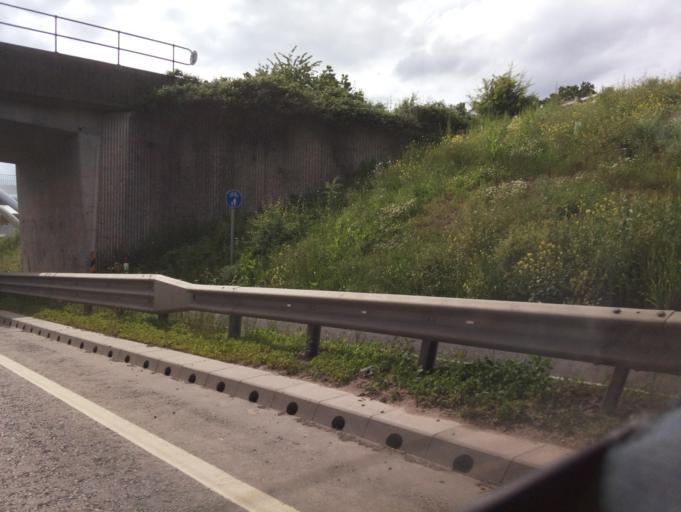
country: GB
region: England
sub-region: Worcestershire
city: Worcester
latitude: 52.1697
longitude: -2.1944
